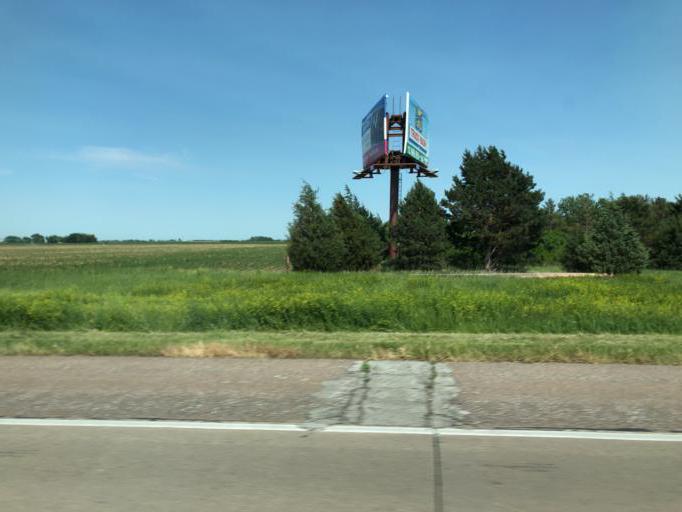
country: US
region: Nebraska
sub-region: Fillmore County
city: Geneva
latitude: 40.6433
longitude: -97.5956
